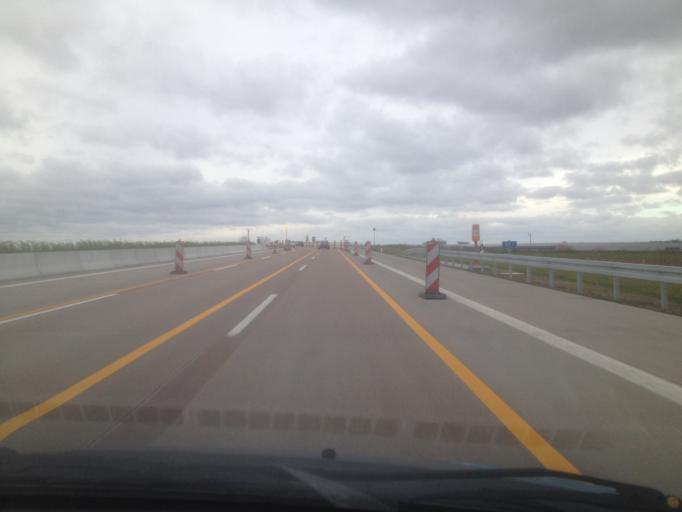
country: DE
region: Bavaria
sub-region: Swabia
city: Rosshaupten
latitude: 48.4108
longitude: 10.4880
